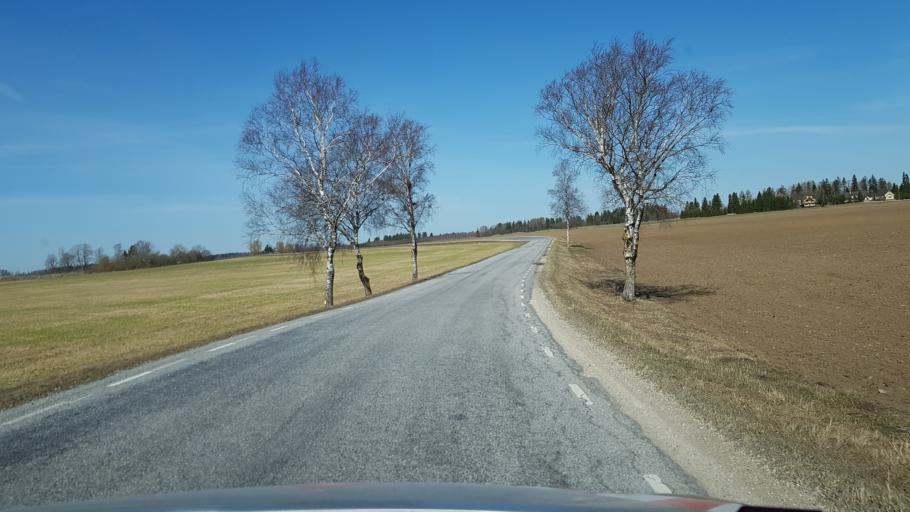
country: EE
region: Laeaene-Virumaa
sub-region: Vinni vald
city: Vinni
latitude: 59.2997
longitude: 26.4155
